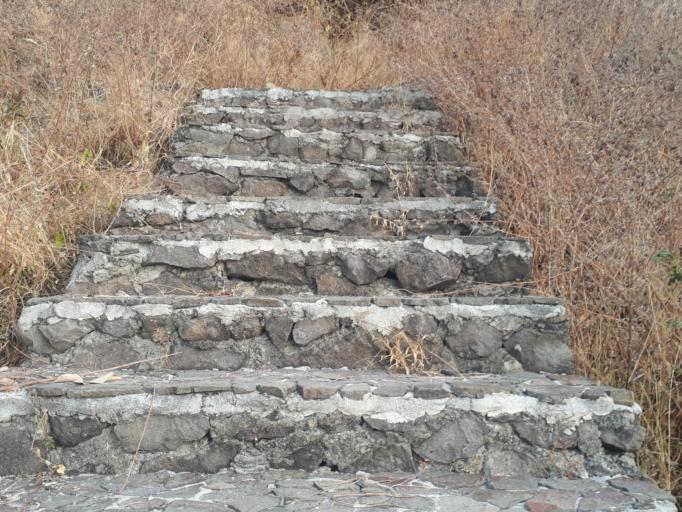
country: ID
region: West Nusa Tenggara
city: Tawun
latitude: -8.7365
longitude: 115.8818
